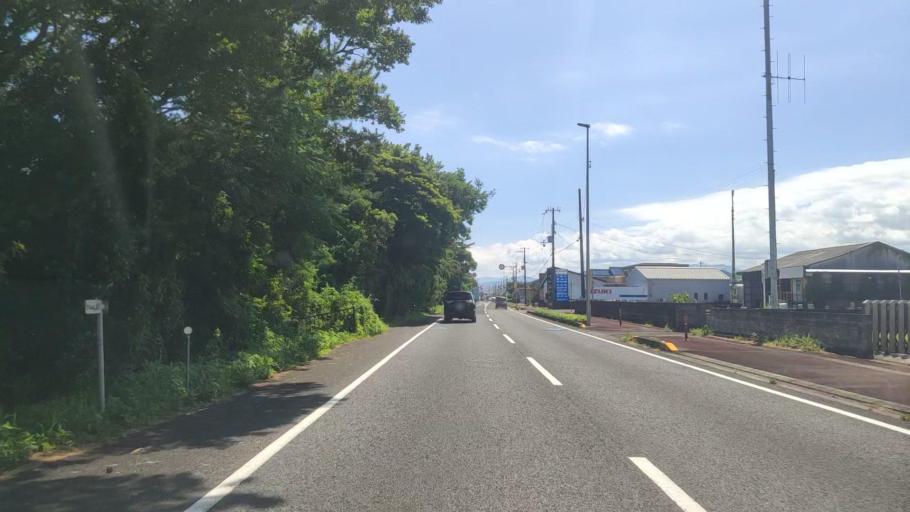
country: JP
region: Wakayama
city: Shingu
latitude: 33.8768
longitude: 136.0906
